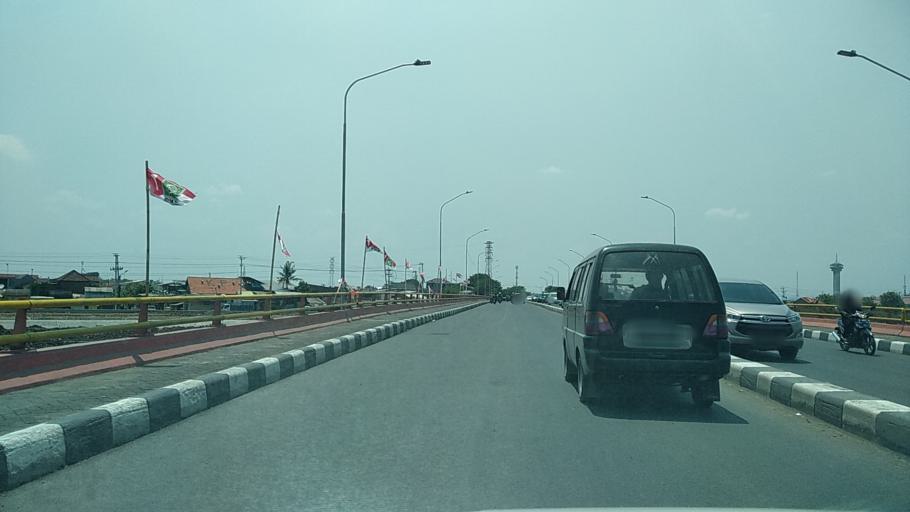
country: ID
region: Central Java
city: Semarang
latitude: -6.9723
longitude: 110.4422
